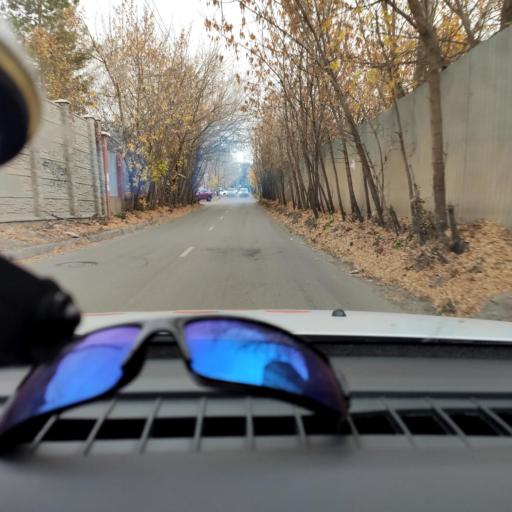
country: RU
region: Samara
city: Samara
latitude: 53.2355
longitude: 50.1762
